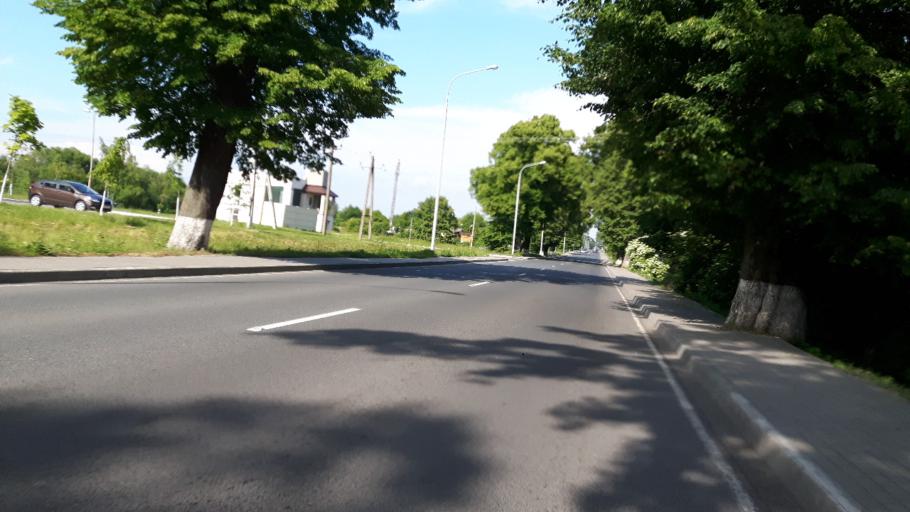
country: RU
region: Kaliningrad
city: Mamonovo
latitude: 54.4630
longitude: 19.9508
